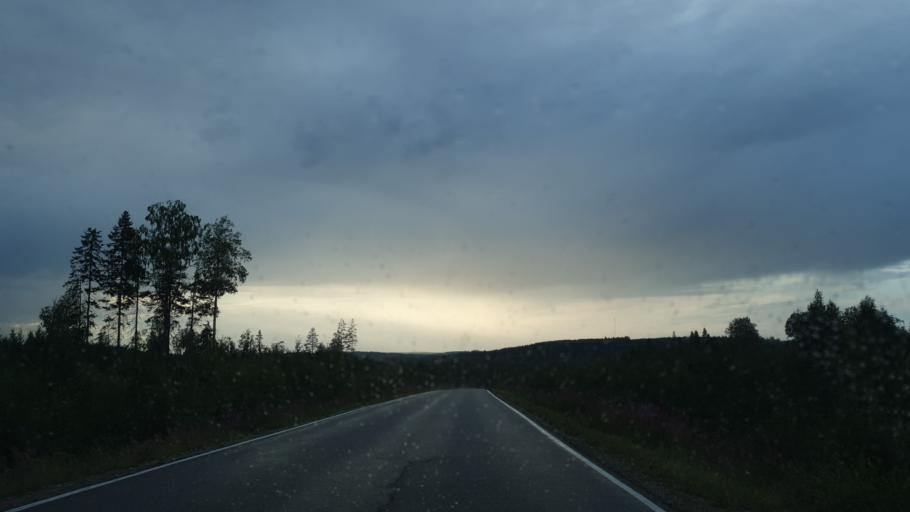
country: FI
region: North Karelia
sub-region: Pielisen Karjala
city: Lieksa
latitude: 63.6121
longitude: 29.8599
